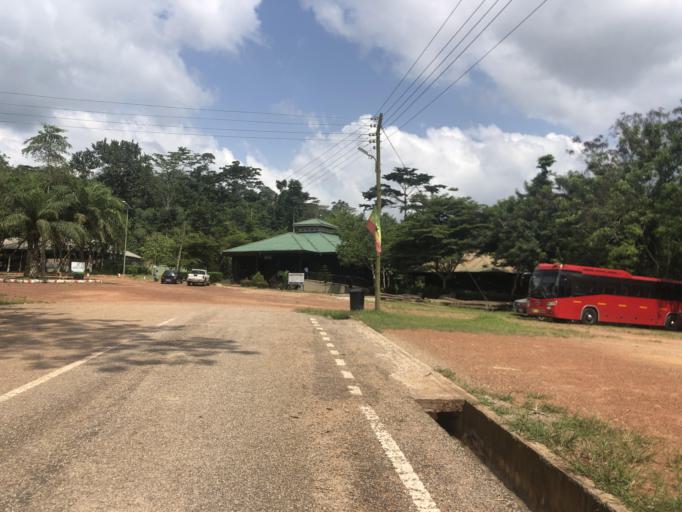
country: GH
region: Central
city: Elmina
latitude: 5.3480
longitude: -1.3832
